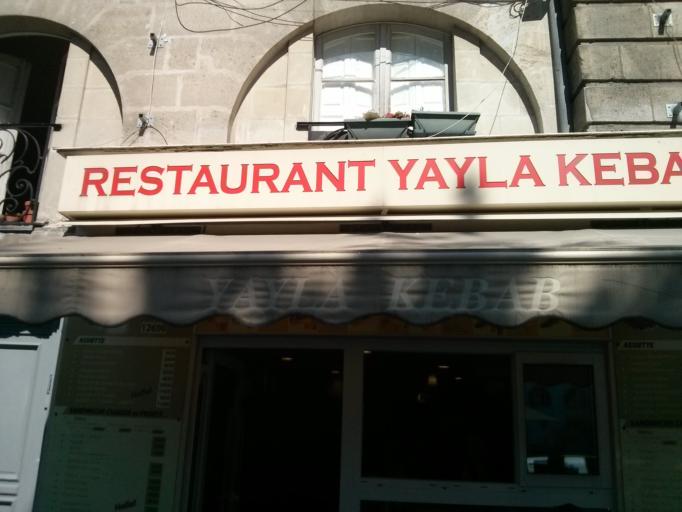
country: FR
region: Pays de la Loire
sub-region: Departement de la Loire-Atlantique
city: Nantes
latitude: 47.2143
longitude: -1.5544
